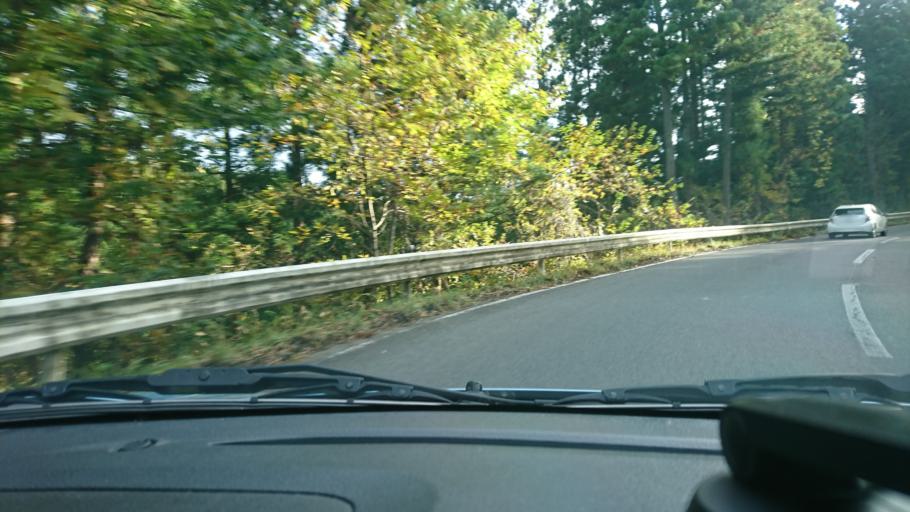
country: JP
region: Miyagi
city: Furukawa
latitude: 38.7379
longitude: 140.8492
